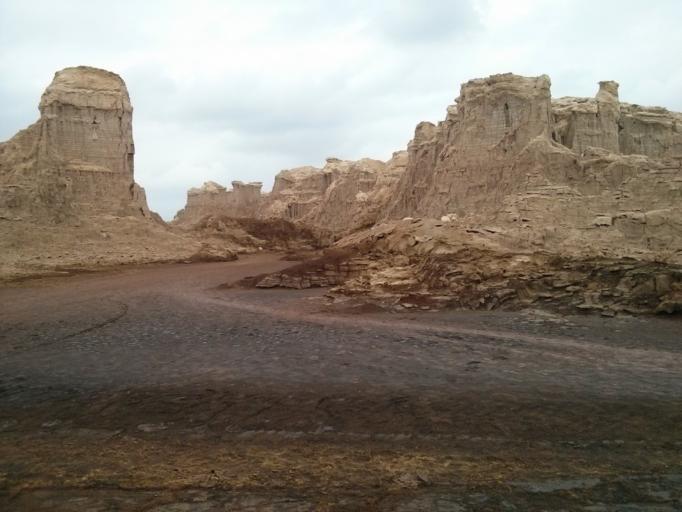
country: ET
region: Tigray
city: Adigrat
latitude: 14.2287
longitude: 40.2902
